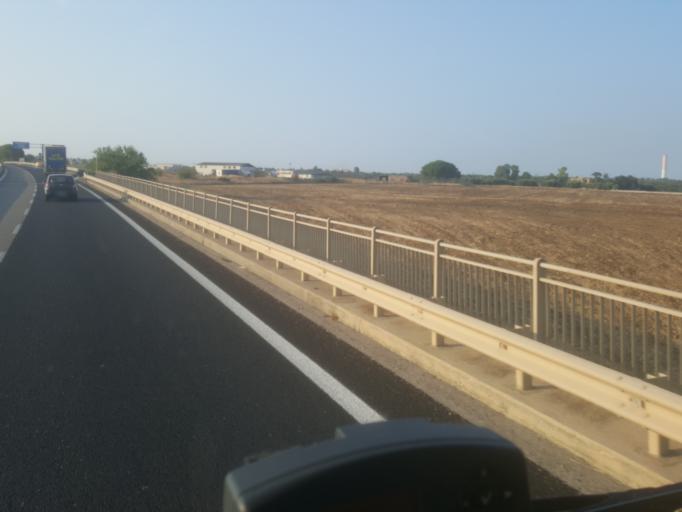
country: IT
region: Latium
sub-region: Citta metropolitana di Roma Capitale
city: Aurelia
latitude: 42.1592
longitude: 11.7888
